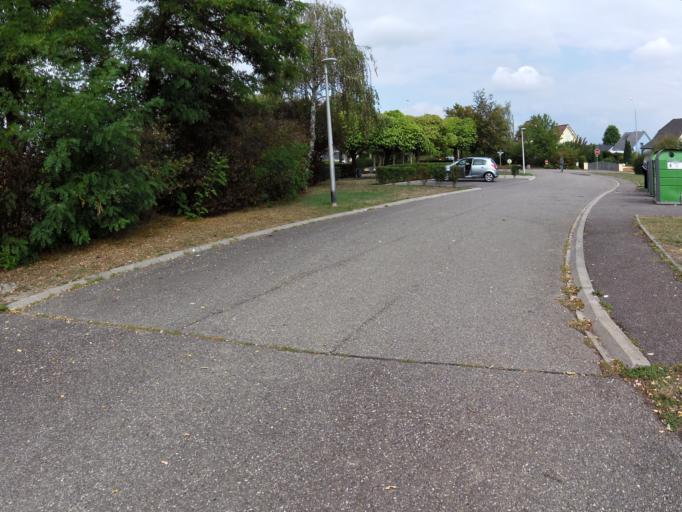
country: FR
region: Alsace
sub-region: Departement du Haut-Rhin
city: Biesheim
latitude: 48.0373
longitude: 7.5398
